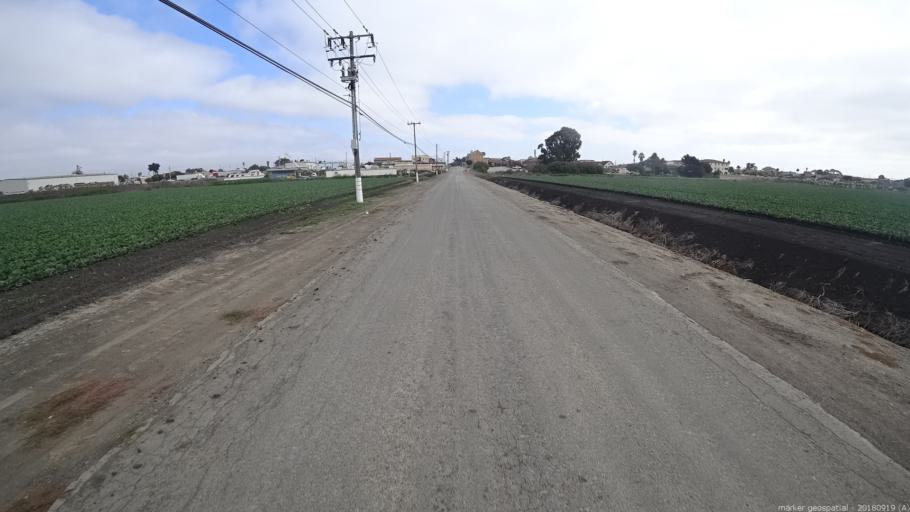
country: US
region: California
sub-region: Monterey County
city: Castroville
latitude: 36.7641
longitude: -121.7607
